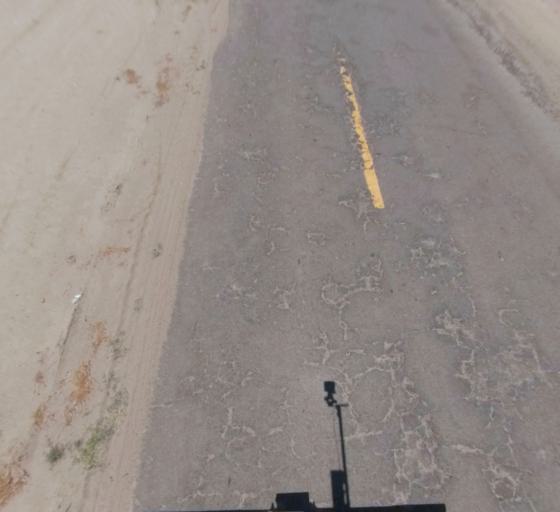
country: US
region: California
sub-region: Madera County
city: Parkwood
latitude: 36.8585
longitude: -120.0893
